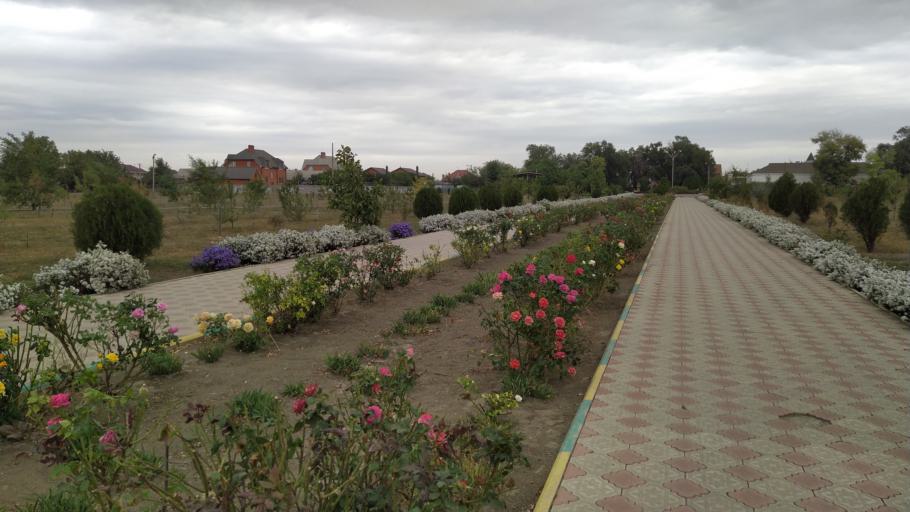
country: RU
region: Rostov
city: Bataysk
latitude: 47.1190
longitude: 39.6762
